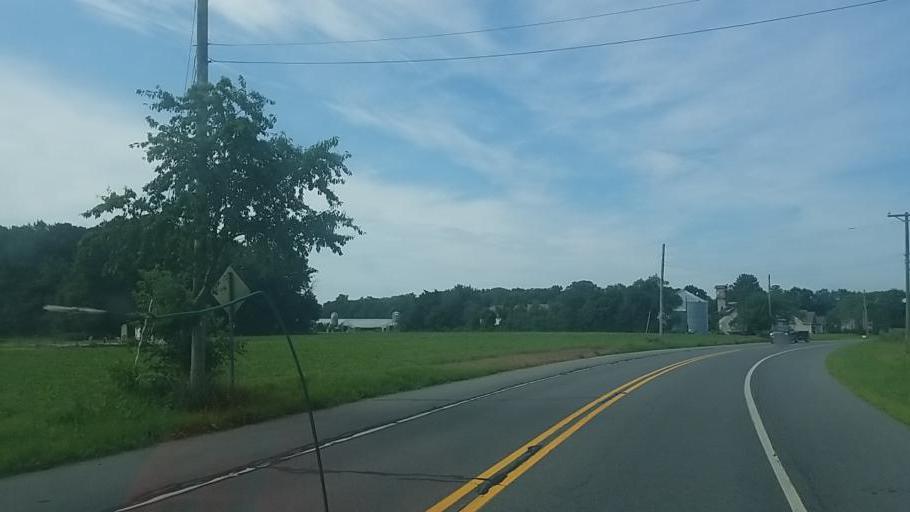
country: US
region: Delaware
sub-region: Sussex County
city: Selbyville
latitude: 38.5309
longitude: -75.1925
